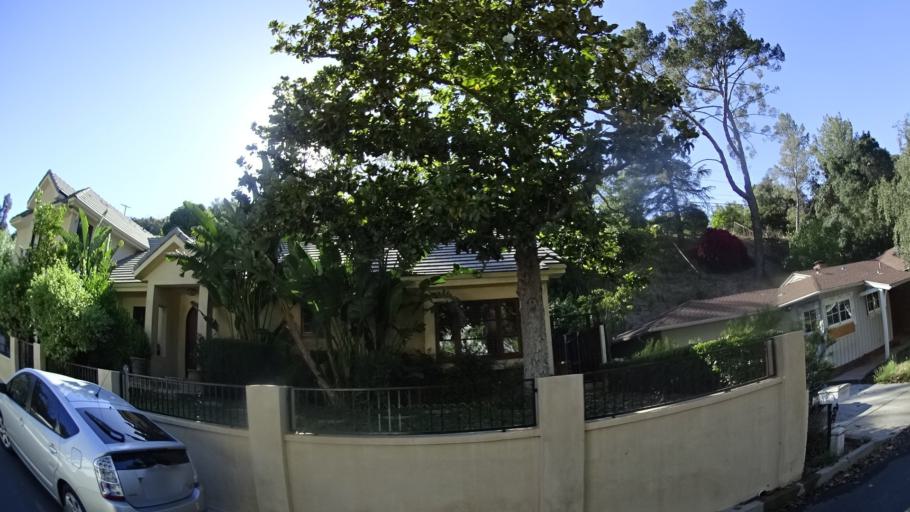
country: US
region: California
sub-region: Los Angeles County
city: Sherman Oaks
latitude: 34.1373
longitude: -118.4507
